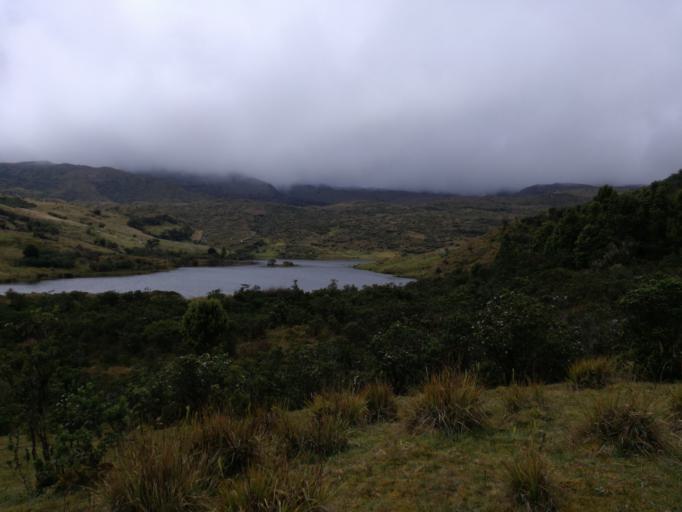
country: CO
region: Boyaca
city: Socha Viejo
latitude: 5.8945
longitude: -72.6770
